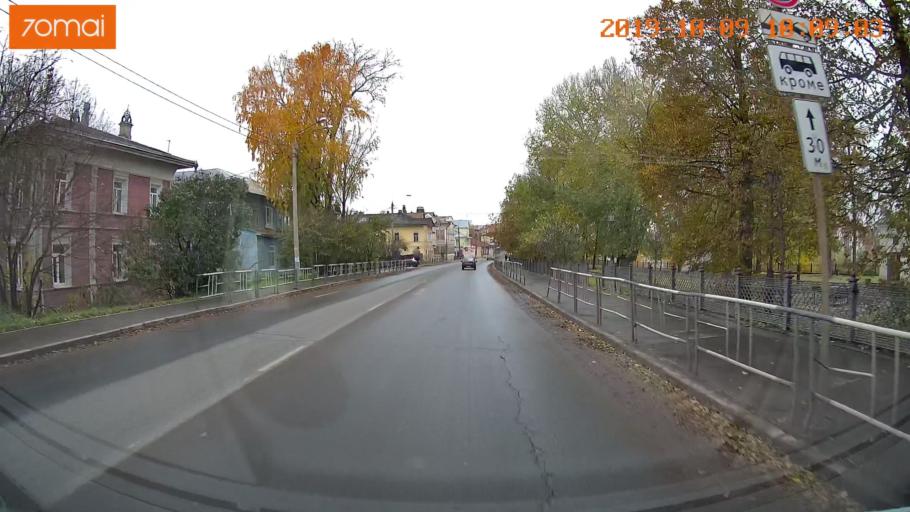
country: RU
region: Vologda
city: Vologda
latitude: 59.2096
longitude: 39.9080
